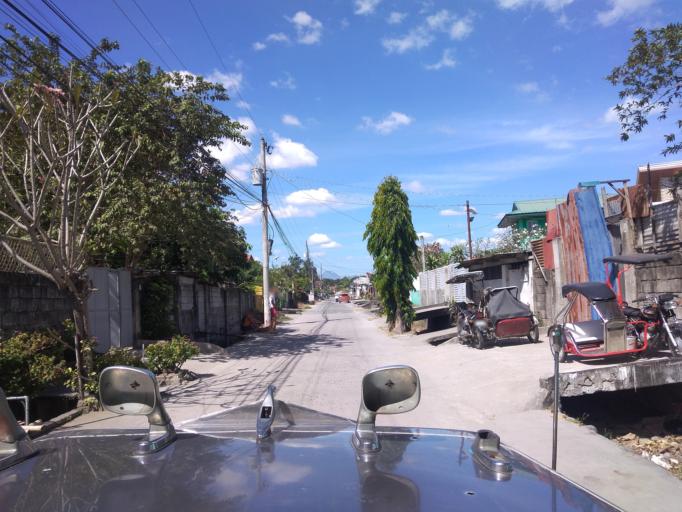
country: PH
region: Central Luzon
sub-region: Province of Pampanga
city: Santa Rita
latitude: 15.0027
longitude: 120.6072
